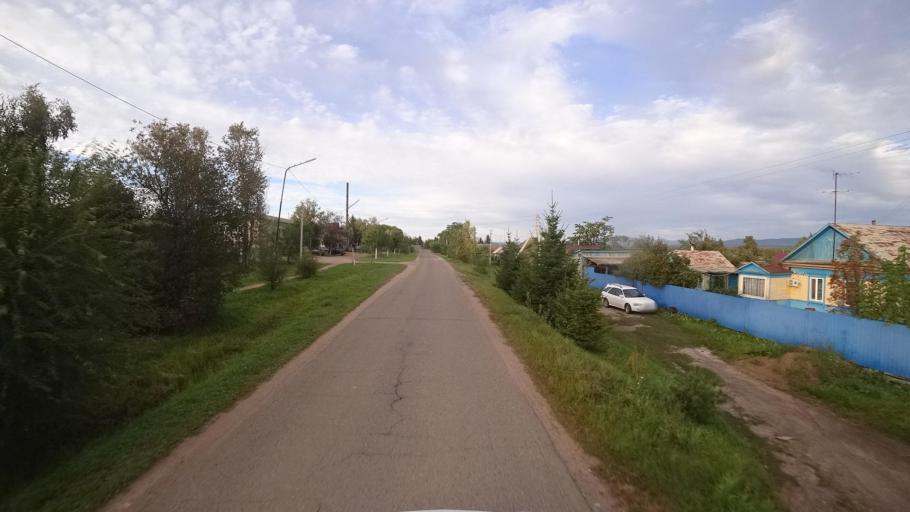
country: RU
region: Primorskiy
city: Yakovlevka
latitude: 44.4218
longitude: 133.4756
